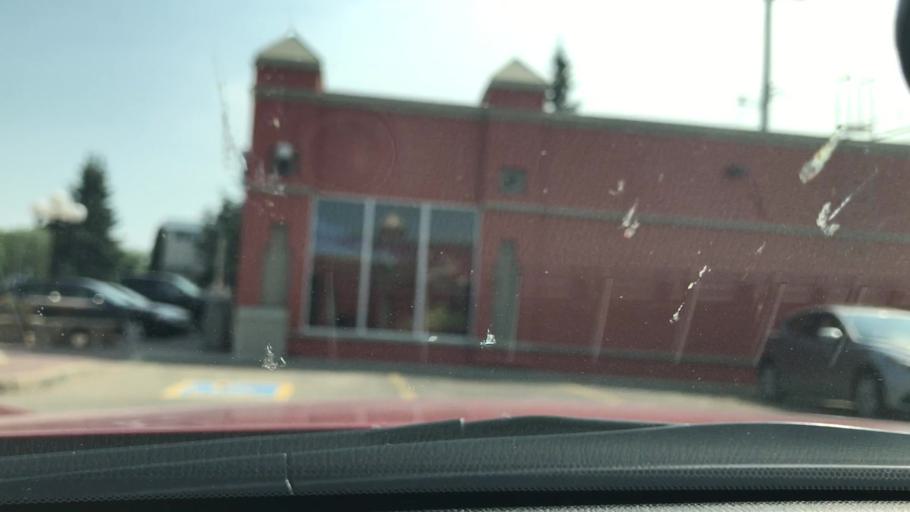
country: CA
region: Alberta
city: Edmonton
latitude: 53.5409
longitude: -113.4376
